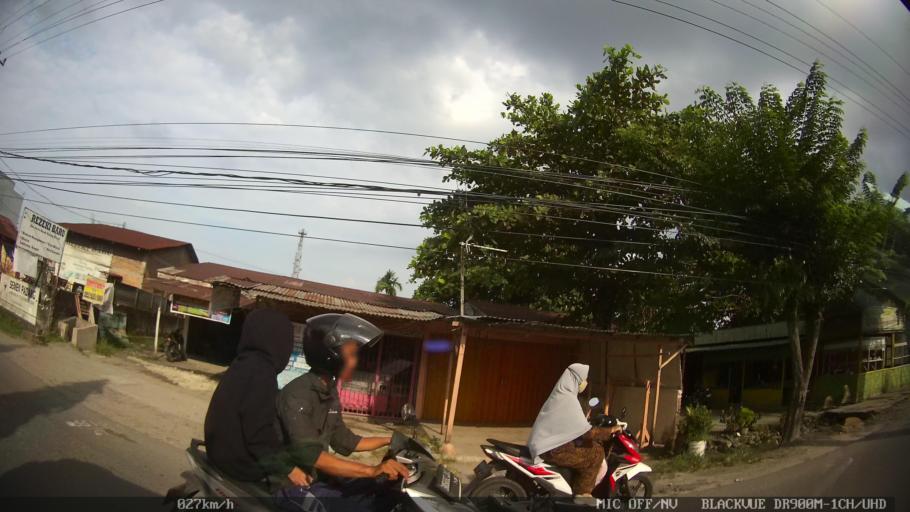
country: ID
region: North Sumatra
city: Sunggal
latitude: 3.5329
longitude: 98.6210
